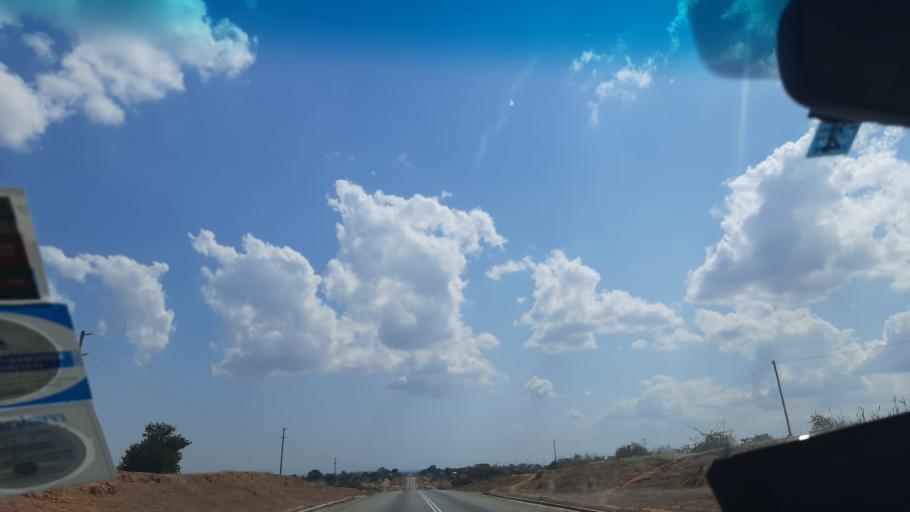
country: TZ
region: Singida
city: Kintinku
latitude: -6.0162
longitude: 35.4444
